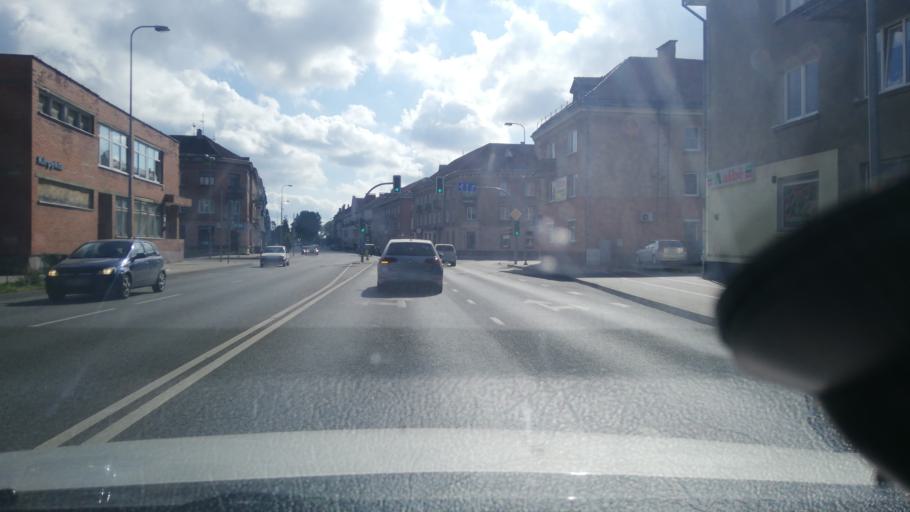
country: LT
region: Klaipedos apskritis
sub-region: Klaipeda
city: Klaipeda
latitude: 55.6788
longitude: 21.1522
